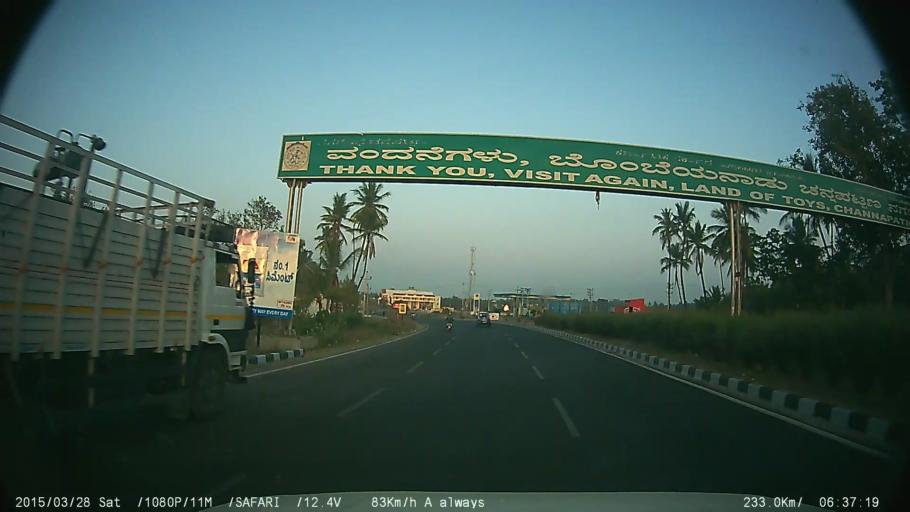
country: IN
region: Karnataka
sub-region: Ramanagara
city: Channapatna
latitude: 12.6486
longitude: 77.1843
